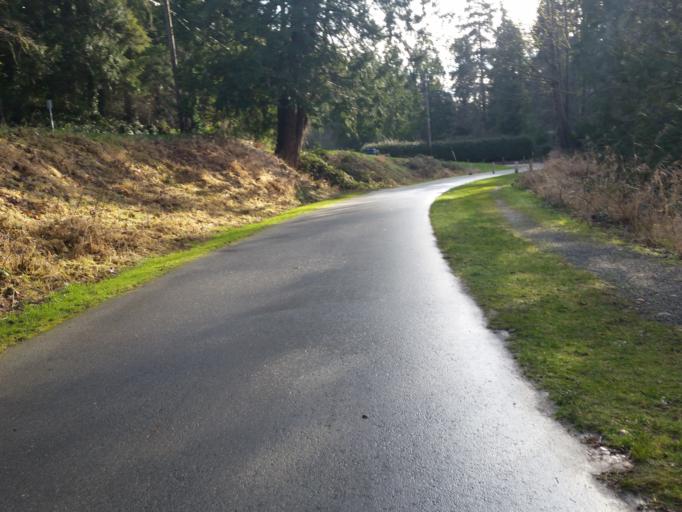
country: US
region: Washington
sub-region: King County
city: Bothell
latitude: 47.7520
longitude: -122.2083
